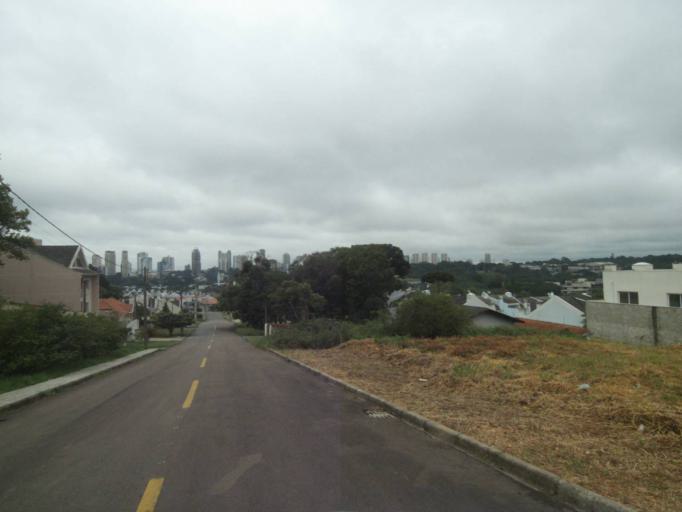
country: BR
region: Parana
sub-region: Curitiba
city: Curitiba
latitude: -25.4251
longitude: -49.3364
